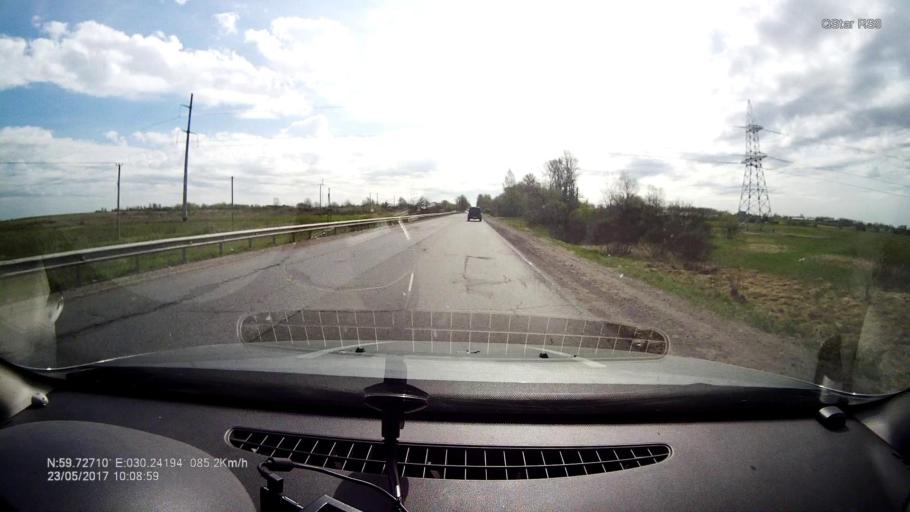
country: RU
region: St.-Petersburg
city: Aleksandrovskaya
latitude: 59.7270
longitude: 30.2424
